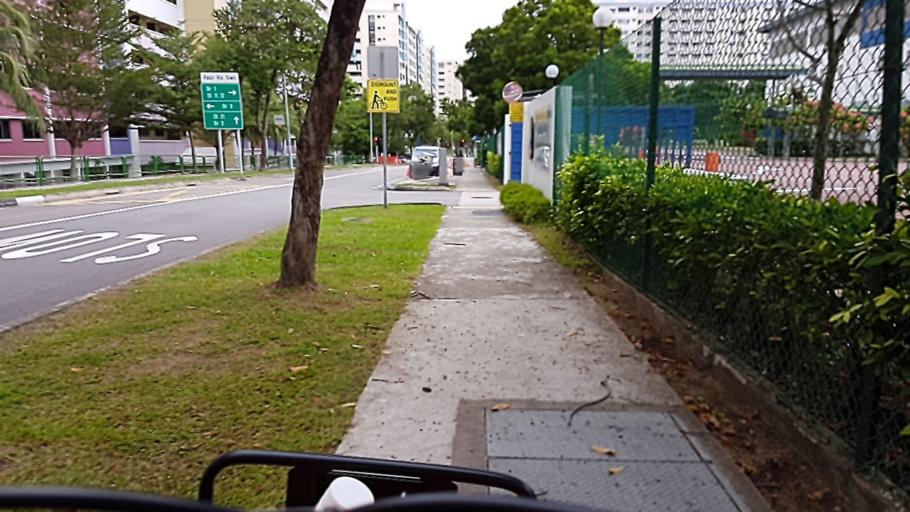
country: MY
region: Johor
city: Kampung Pasir Gudang Baru
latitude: 1.3736
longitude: 103.9593
